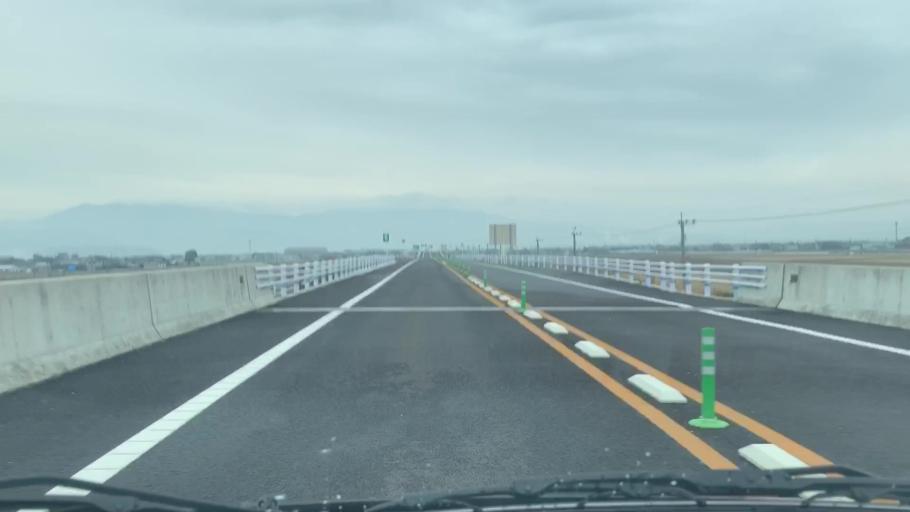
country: JP
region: Saga Prefecture
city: Saga-shi
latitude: 33.2099
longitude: 130.2149
